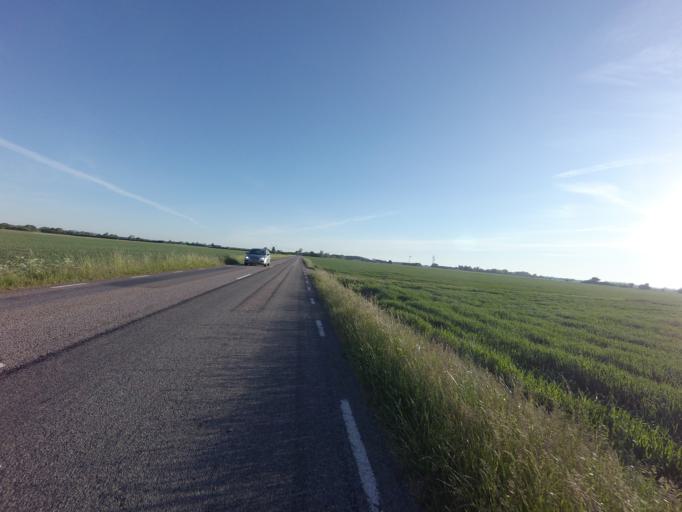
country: SE
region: Skane
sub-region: Helsingborg
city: Odakra
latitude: 56.1852
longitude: 12.6761
